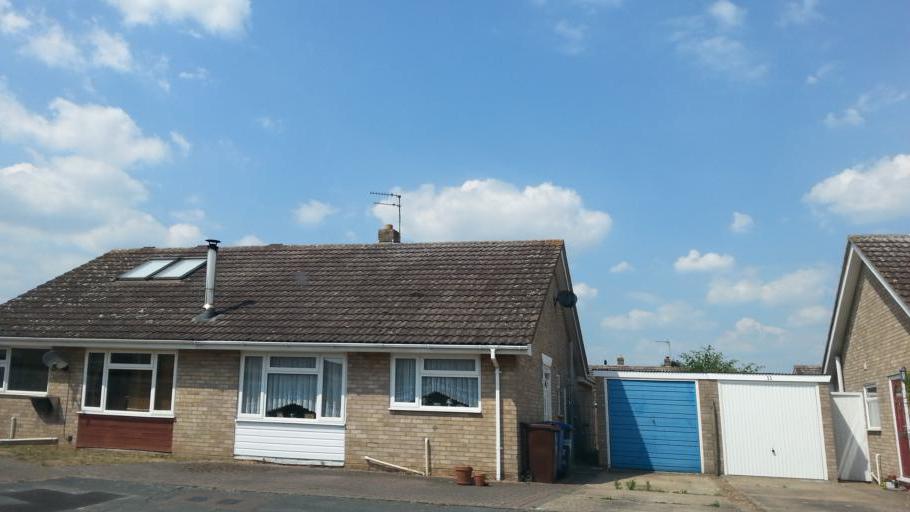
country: GB
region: England
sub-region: Cambridgeshire
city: Isleham
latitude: 52.3045
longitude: 0.4927
